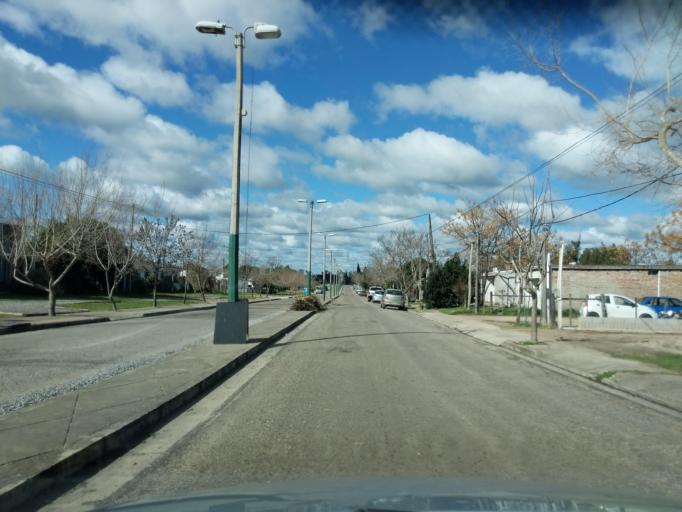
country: UY
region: Florida
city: Florida
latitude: -34.0921
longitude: -56.2383
